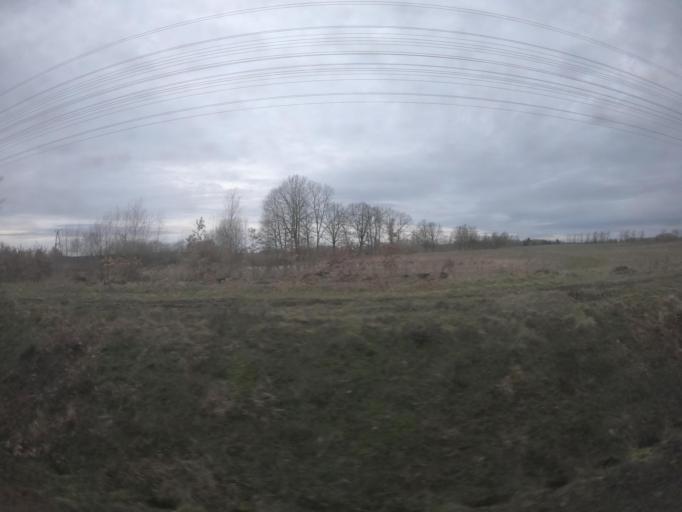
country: PL
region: West Pomeranian Voivodeship
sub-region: Powiat szczecinecki
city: Borne Sulinowo
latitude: 53.6290
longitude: 16.4796
